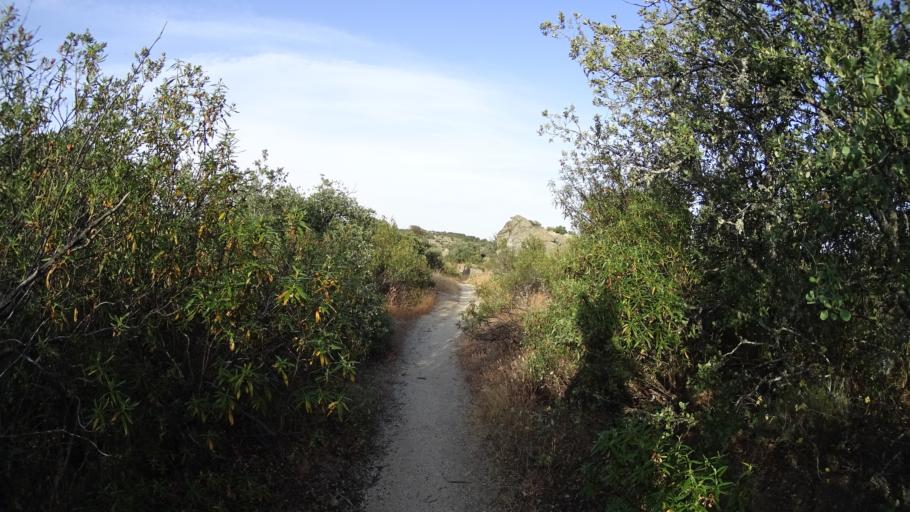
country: ES
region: Madrid
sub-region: Provincia de Madrid
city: Torrelodones
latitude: 40.5911
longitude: -3.9412
